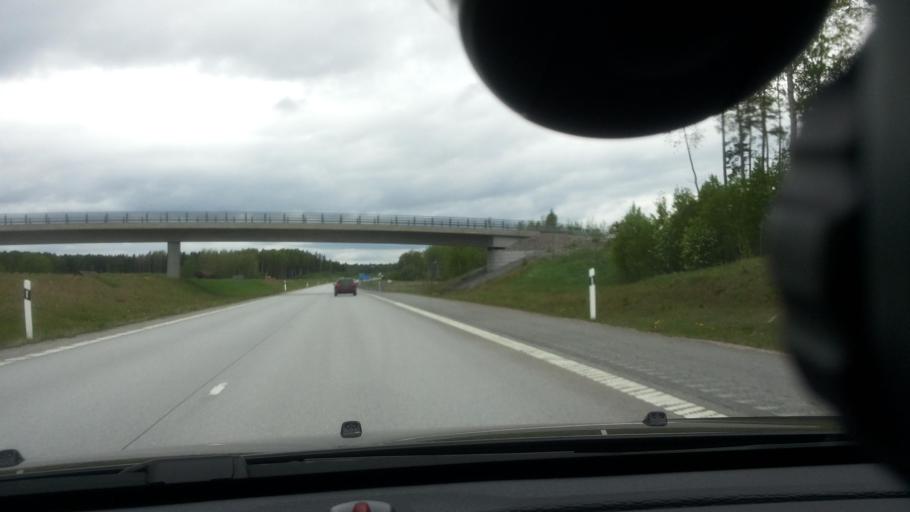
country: SE
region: Uppsala
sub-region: Uppsala Kommun
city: Storvreta
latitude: 60.0005
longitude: 17.6332
